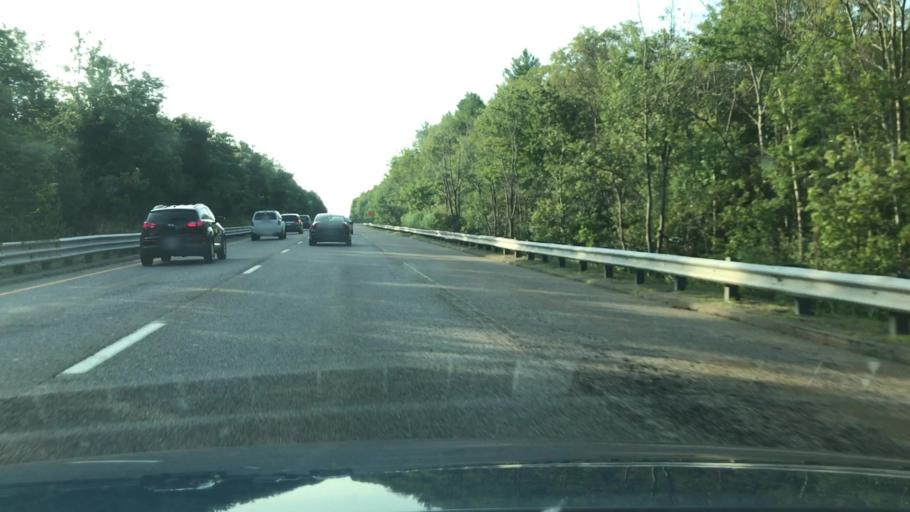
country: US
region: Massachusetts
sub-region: Plymouth County
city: Hanover
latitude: 42.1354
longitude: -70.8163
